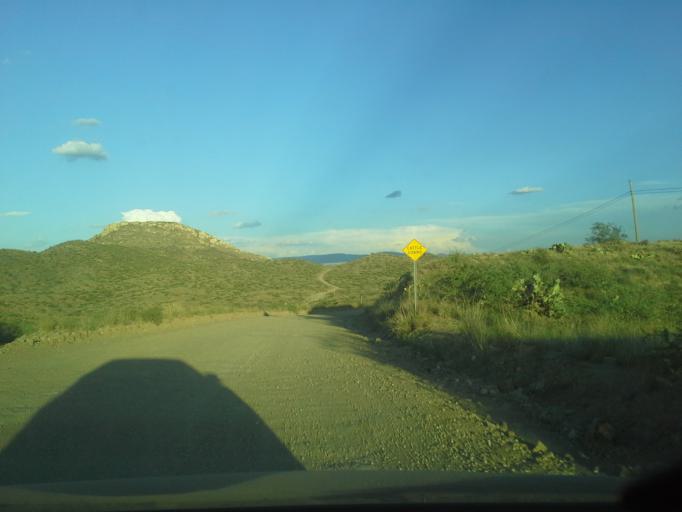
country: US
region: Arizona
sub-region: Yavapai County
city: Spring Valley
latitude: 34.2782
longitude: -112.2301
